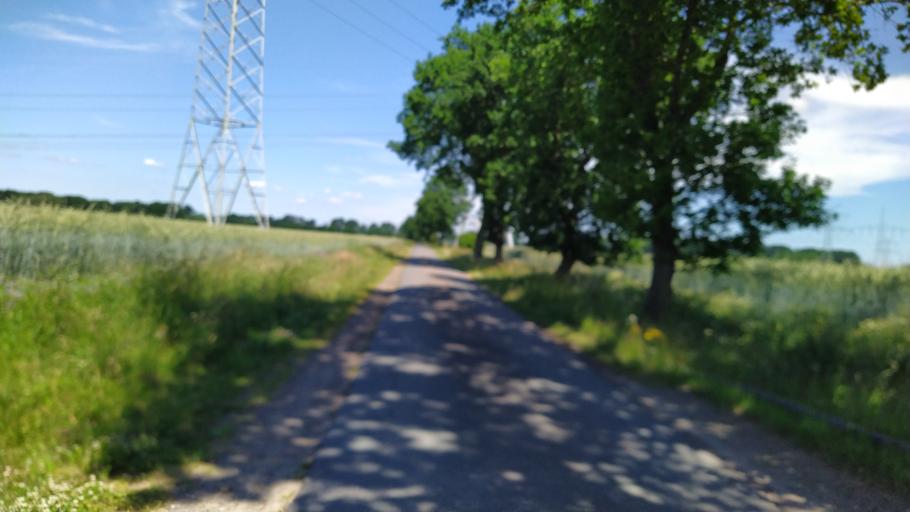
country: DE
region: Lower Saxony
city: Deinste
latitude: 53.5101
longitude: 9.4402
